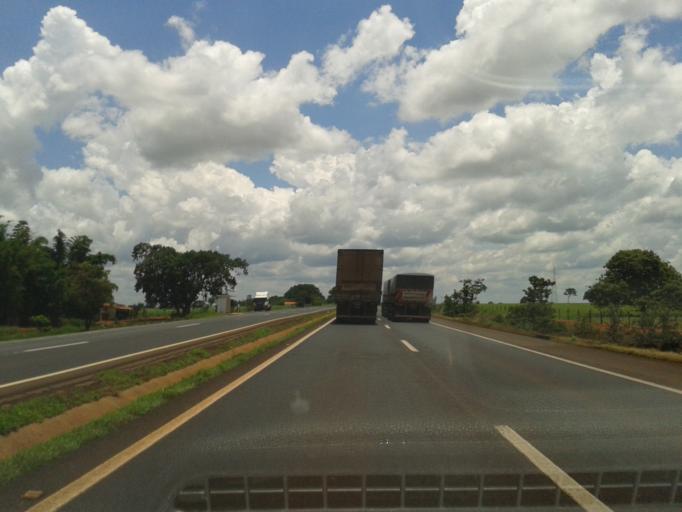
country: BR
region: Minas Gerais
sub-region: Centralina
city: Centralina
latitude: -18.6710
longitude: -49.1610
